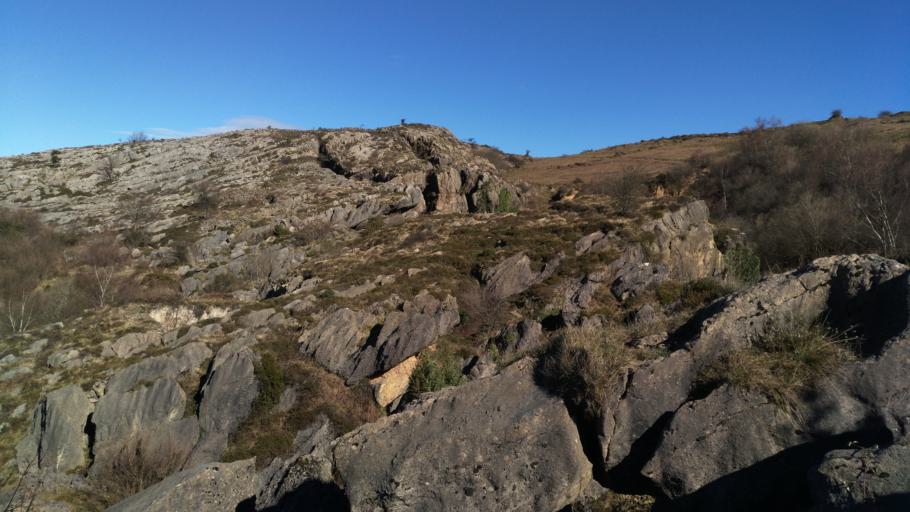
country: ES
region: Basque Country
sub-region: Bizkaia
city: Guenes
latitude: 43.2618
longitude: -3.0805
